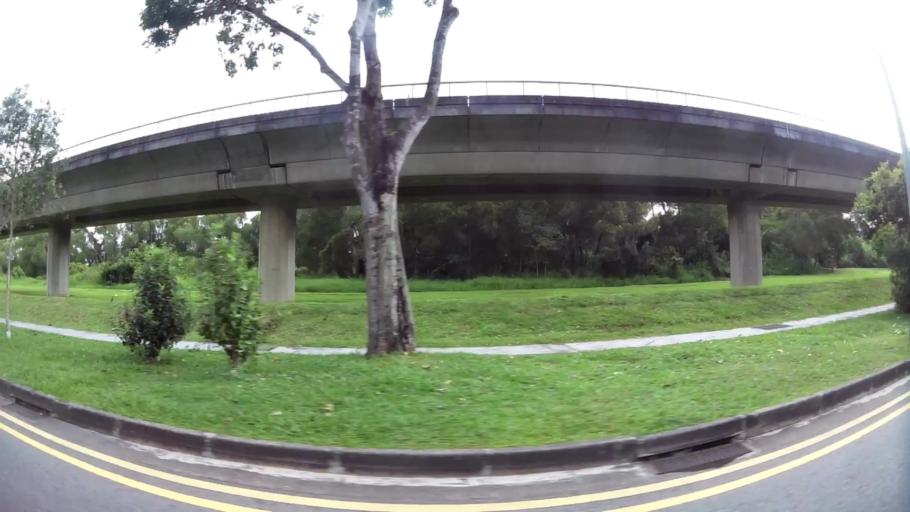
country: SG
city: Singapore
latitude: 1.3623
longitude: 103.9449
